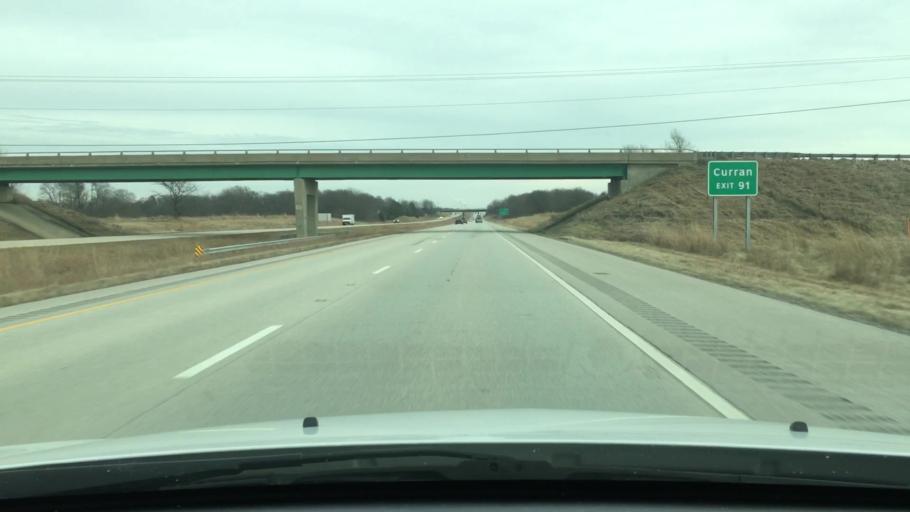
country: US
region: Illinois
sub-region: Sangamon County
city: Jerome
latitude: 39.7517
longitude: -89.7726
